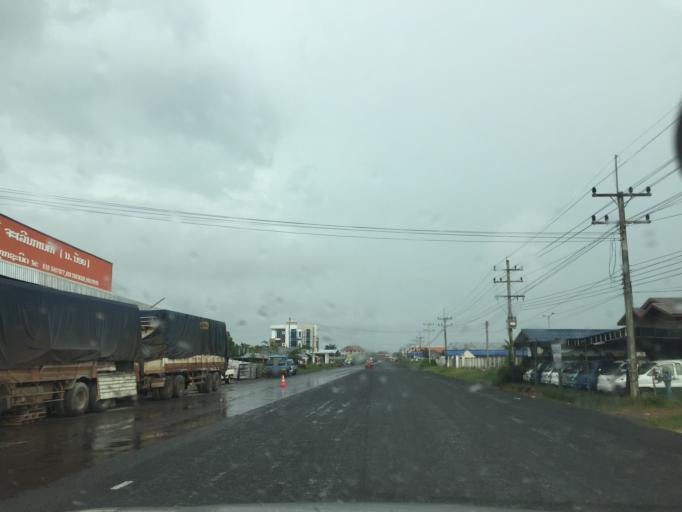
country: LA
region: Attapu
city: Attapu
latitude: 14.8253
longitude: 106.8083
